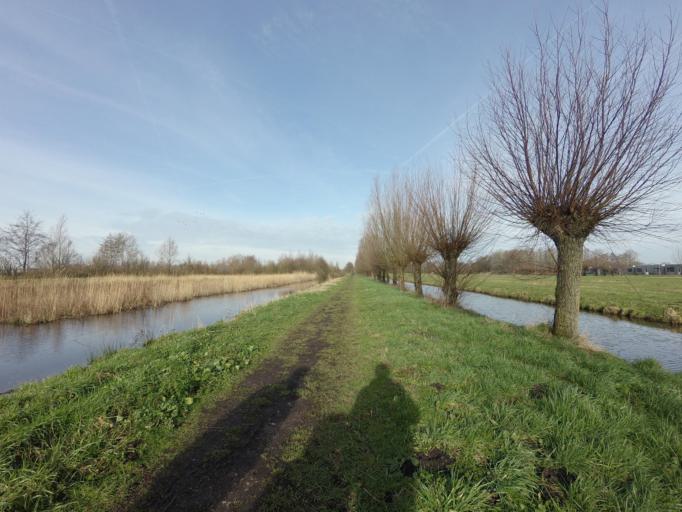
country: NL
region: Utrecht
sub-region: Gemeente Woerden
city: Woerden
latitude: 52.0904
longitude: 4.9251
